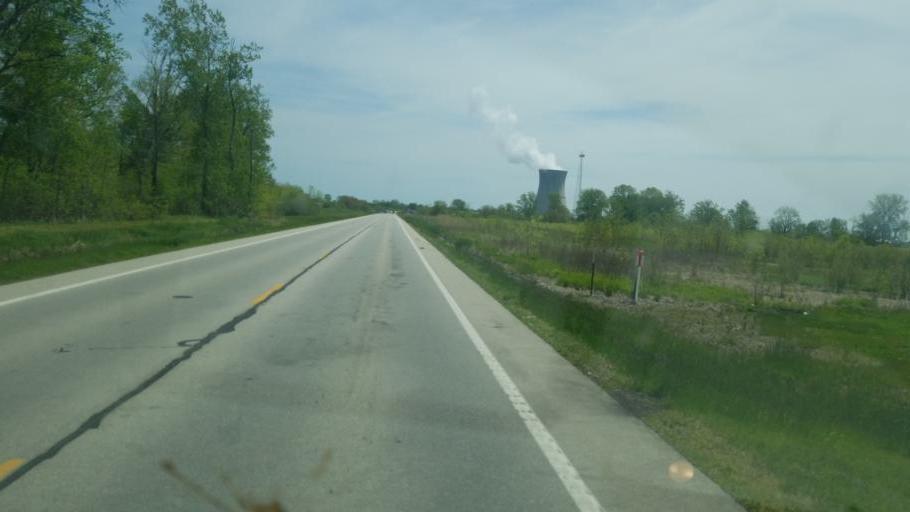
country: US
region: Ohio
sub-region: Ottawa County
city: Oak Harbor
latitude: 41.6038
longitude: -83.1155
